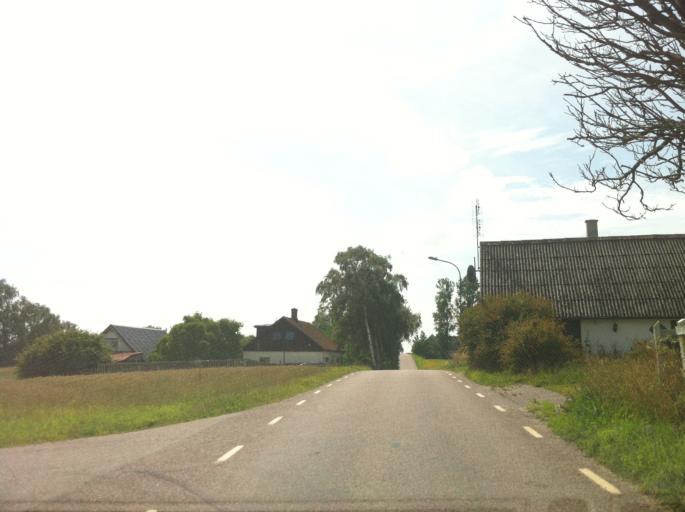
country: SE
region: Skane
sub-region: Skurups Kommun
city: Skurup
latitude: 55.4400
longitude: 13.4440
